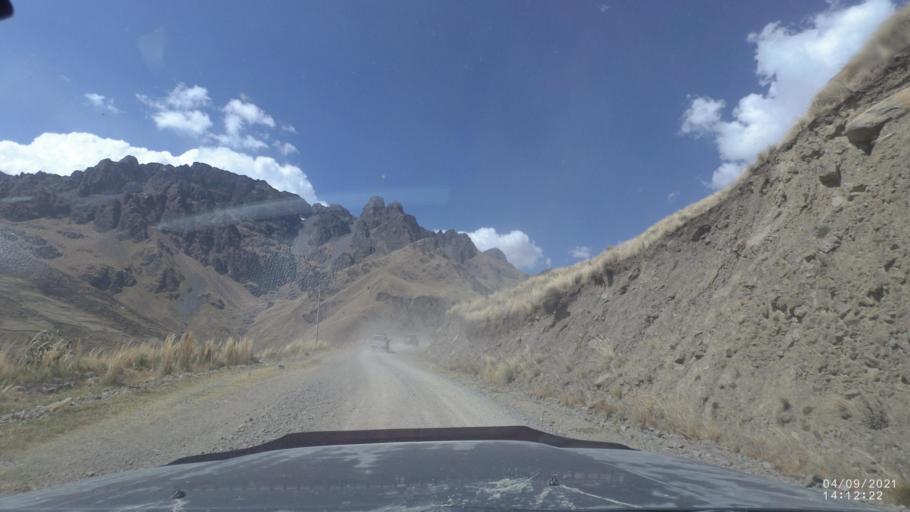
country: BO
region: Cochabamba
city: Sipe Sipe
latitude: -17.2245
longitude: -66.4522
